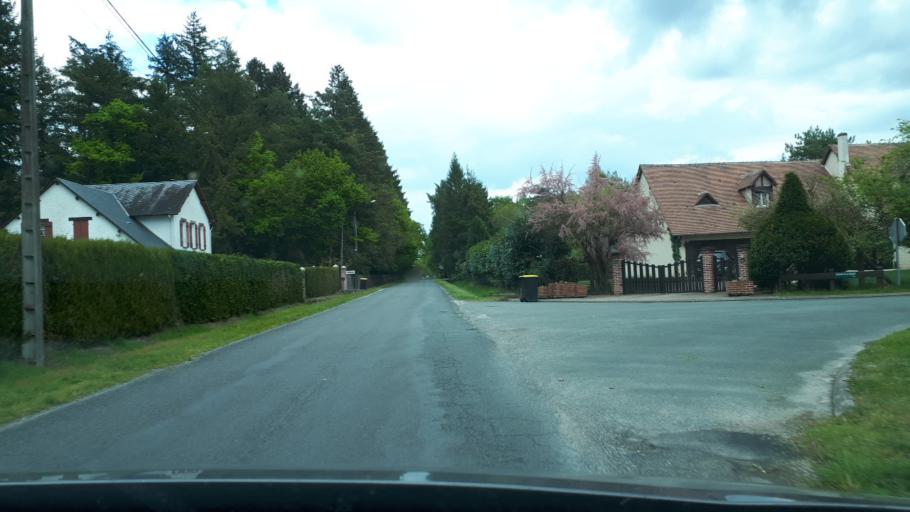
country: FR
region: Centre
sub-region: Departement du Loir-et-Cher
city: Nouan-le-Fuzelier
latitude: 47.5346
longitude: 2.0478
